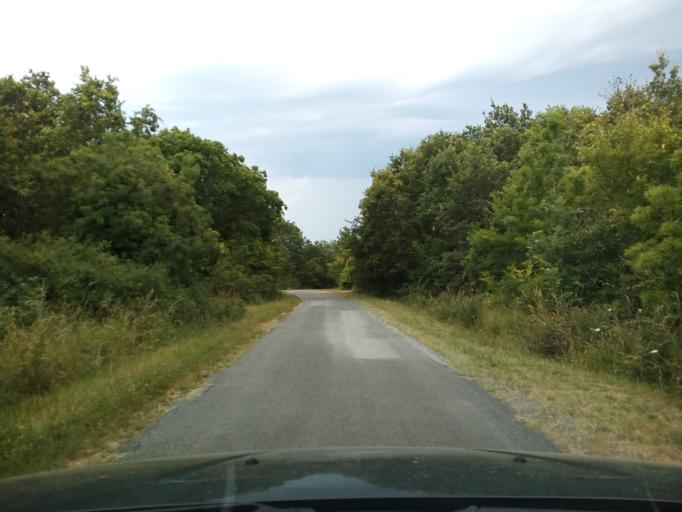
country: FR
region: Poitou-Charentes
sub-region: Departement de la Charente-Maritime
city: Dolus-d'Oleron
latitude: 45.9303
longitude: -1.2631
